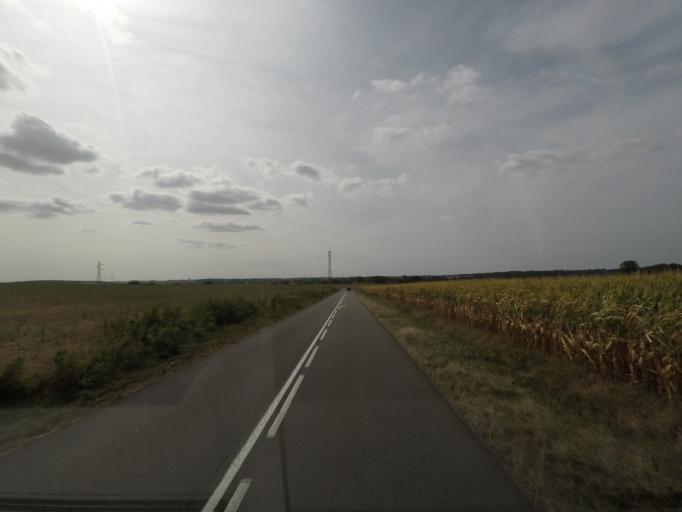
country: FR
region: Poitou-Charentes
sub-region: Departement de la Charente
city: Ruffec
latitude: 46.0251
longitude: 0.2426
